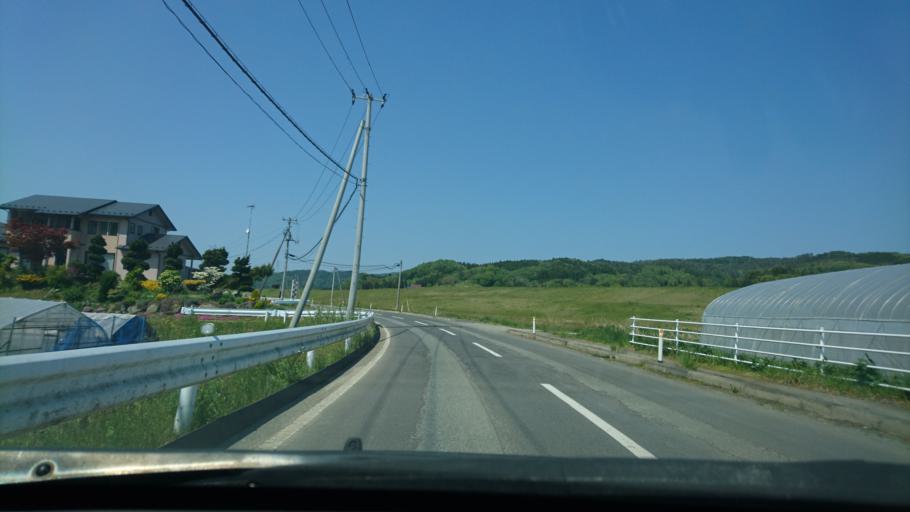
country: JP
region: Iwate
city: Ichinoseki
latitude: 38.9057
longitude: 141.2561
